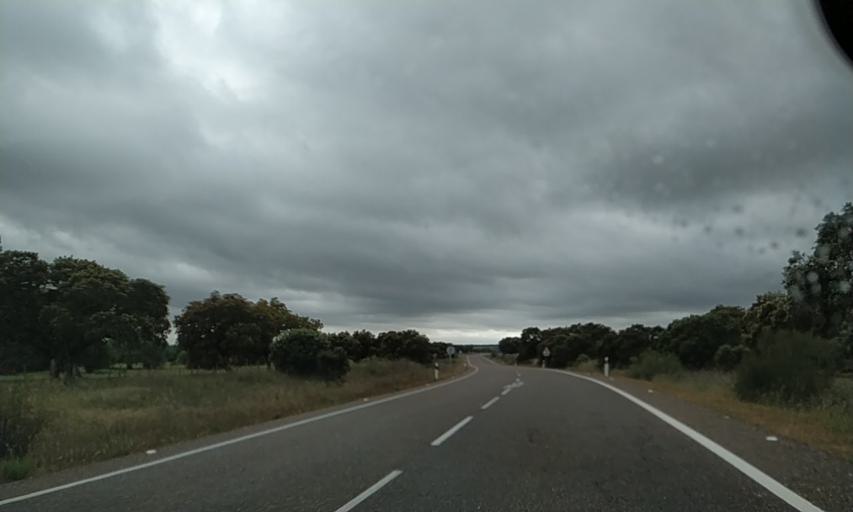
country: ES
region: Extremadura
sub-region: Provincia de Badajoz
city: La Roca de la Sierra
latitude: 39.0690
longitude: -6.7585
